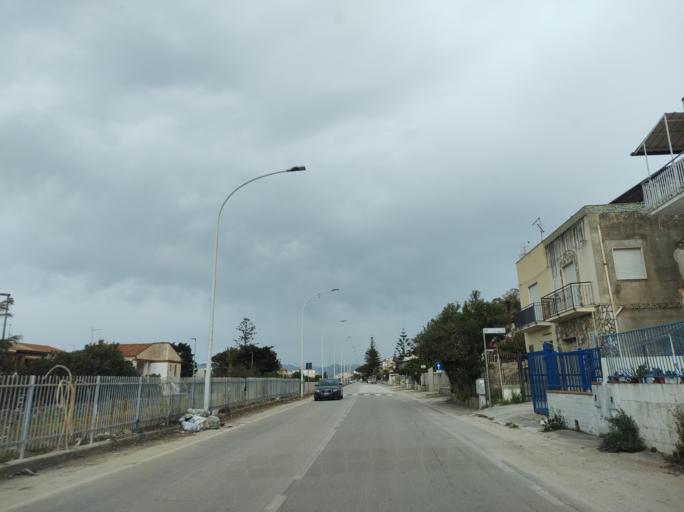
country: IT
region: Sicily
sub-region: Trapani
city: Alcamo
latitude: 38.0265
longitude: 12.9301
